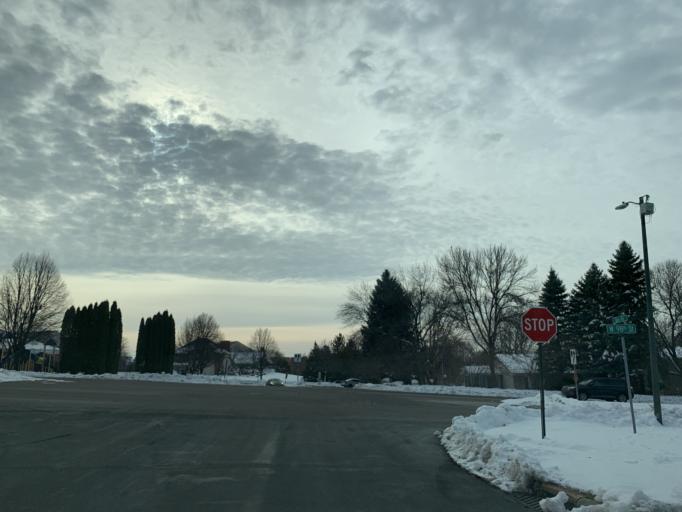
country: US
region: Minnesota
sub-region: Scott County
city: Savage
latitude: 44.8264
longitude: -93.3531
